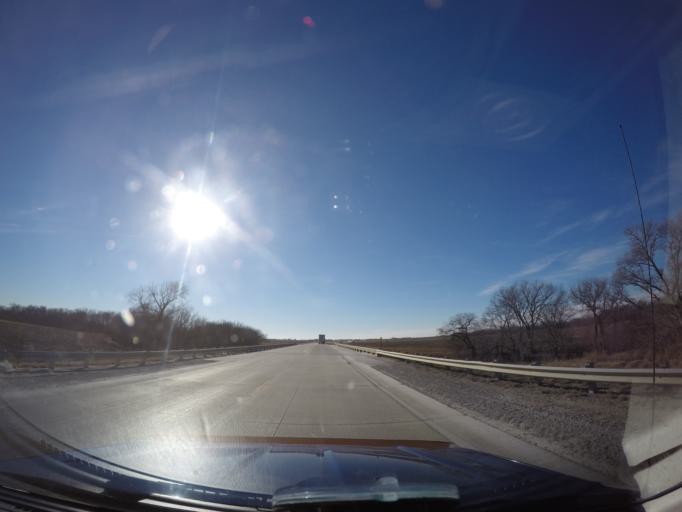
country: US
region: Kansas
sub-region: Marion County
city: Marion
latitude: 38.3613
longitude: -97.0694
